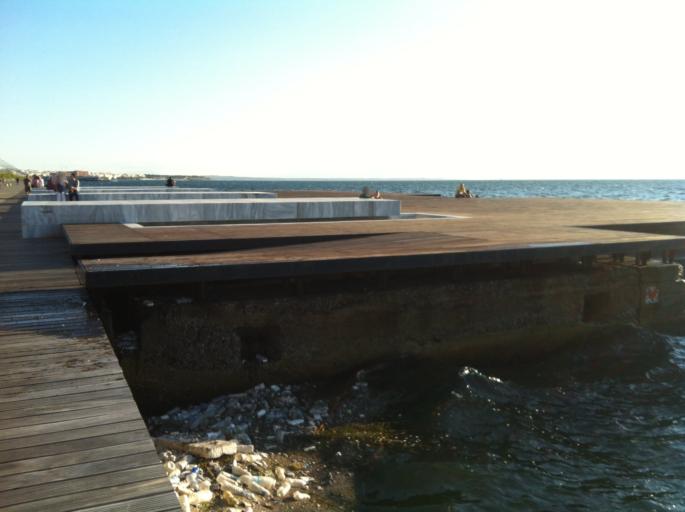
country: GR
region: Central Macedonia
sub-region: Nomos Thessalonikis
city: Agios Pavlos
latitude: 40.6181
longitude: 22.9515
